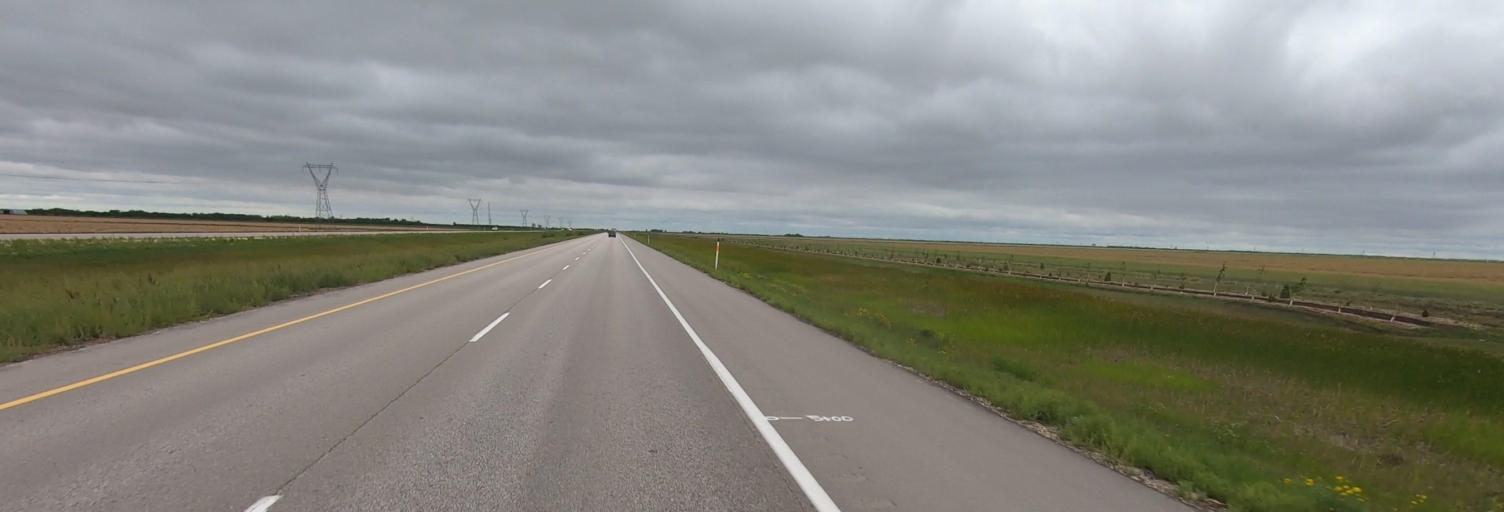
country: CA
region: Manitoba
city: Headingley
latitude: 49.8871
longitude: -97.6072
